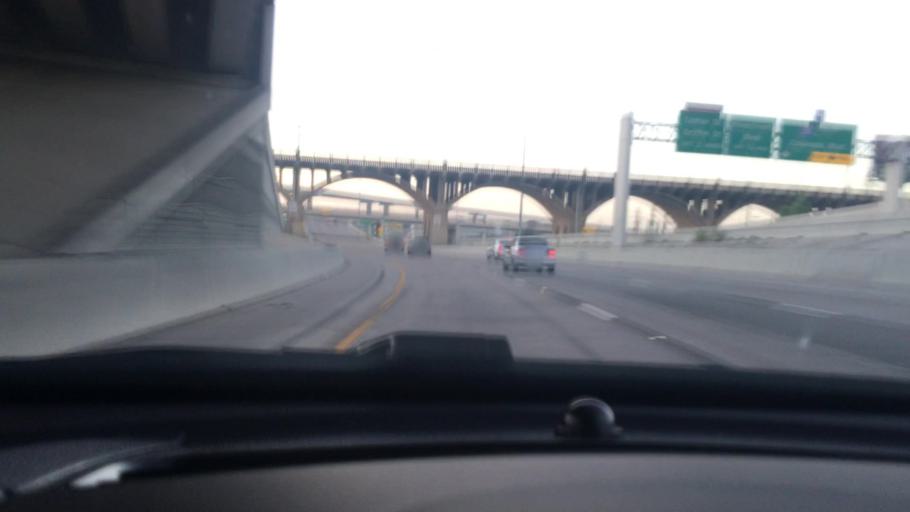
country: US
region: Texas
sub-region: Dallas County
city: Dallas
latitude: 32.7707
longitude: -96.8101
